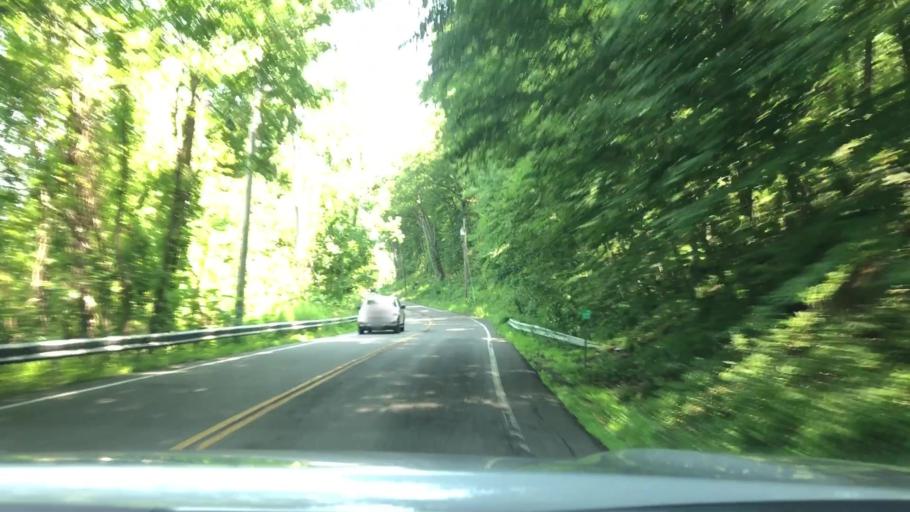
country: US
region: New York
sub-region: Orange County
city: Fort Montgomery
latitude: 41.3243
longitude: -73.9734
